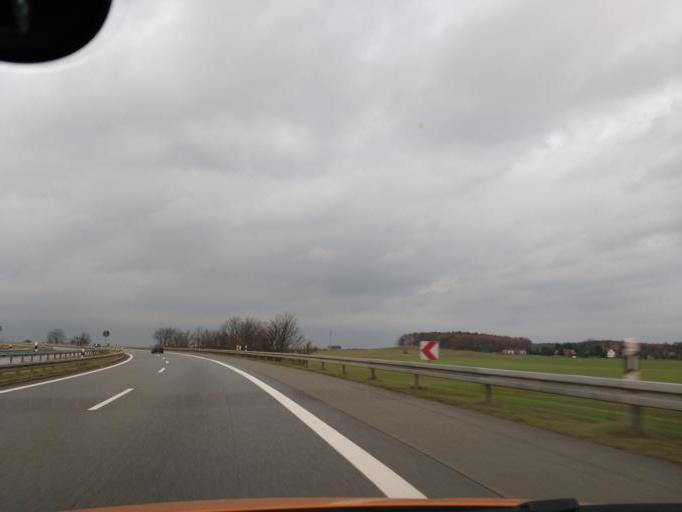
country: DE
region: Brandenburg
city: Wittstock
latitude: 53.1296
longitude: 12.4661
